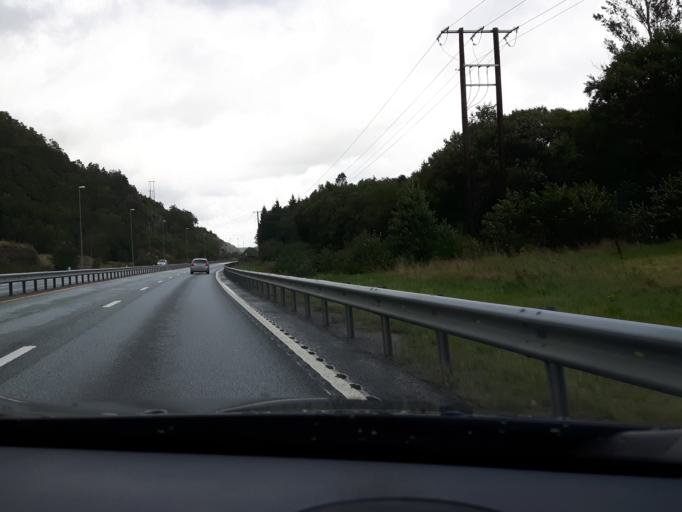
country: NO
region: Vest-Agder
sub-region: Sogne
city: Tangvall
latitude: 58.1111
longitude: 7.8331
